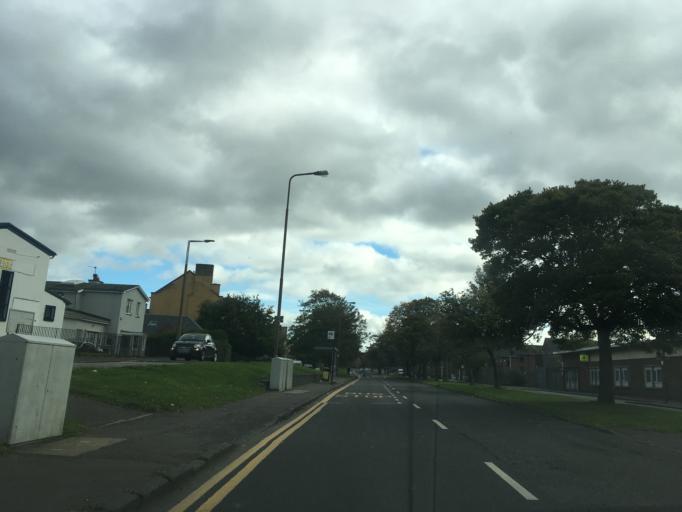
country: GB
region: Scotland
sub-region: Edinburgh
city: Edinburgh
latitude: 55.9706
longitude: -3.2512
